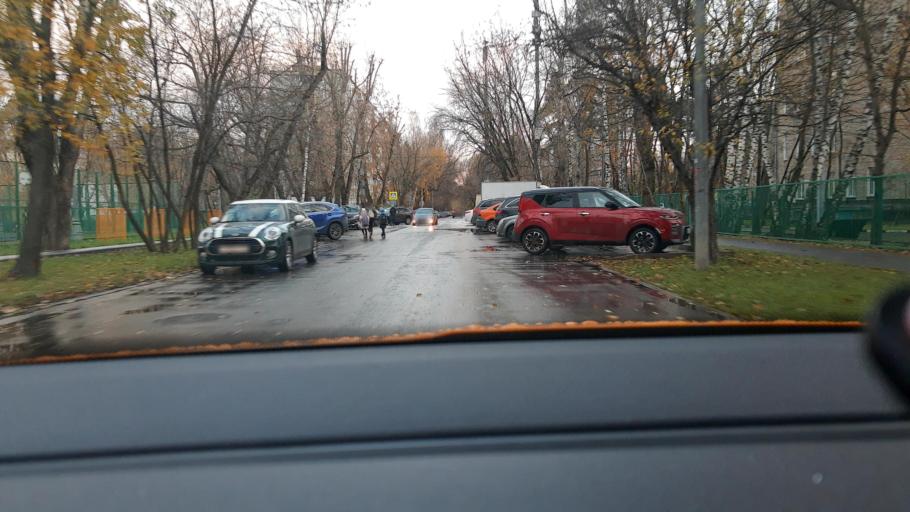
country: RU
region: Moscow
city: Vatutino
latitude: 55.8838
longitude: 37.6961
